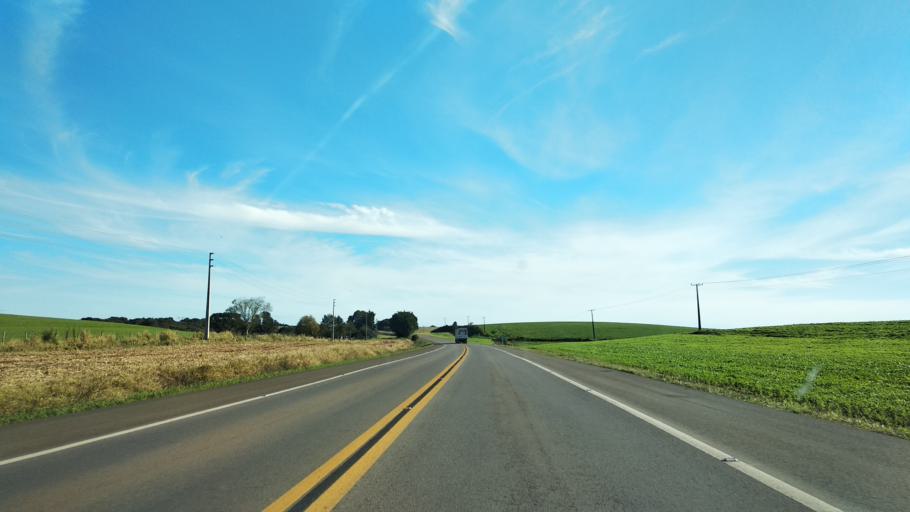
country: BR
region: Santa Catarina
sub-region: Campos Novos
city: Campos Novos
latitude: -27.4921
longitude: -51.3332
